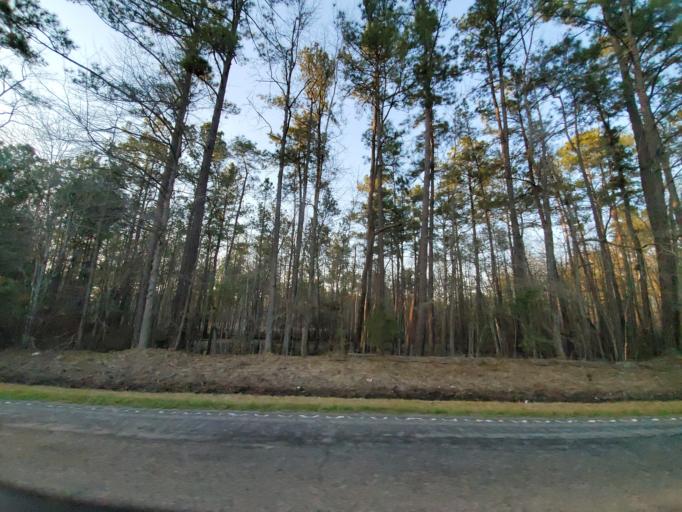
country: US
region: South Carolina
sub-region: Dorchester County
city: Saint George
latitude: 33.0474
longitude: -80.5693
